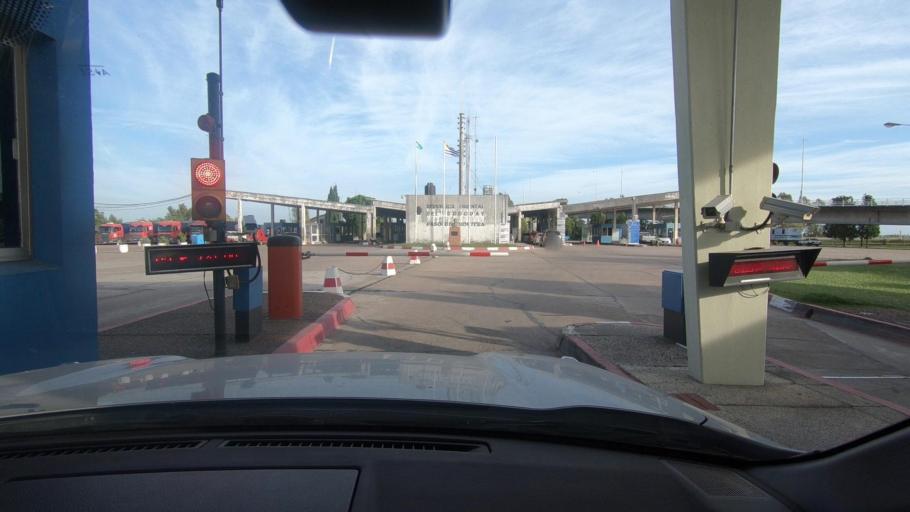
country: AR
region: Entre Rios
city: Colon
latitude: -32.2544
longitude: -58.1397
